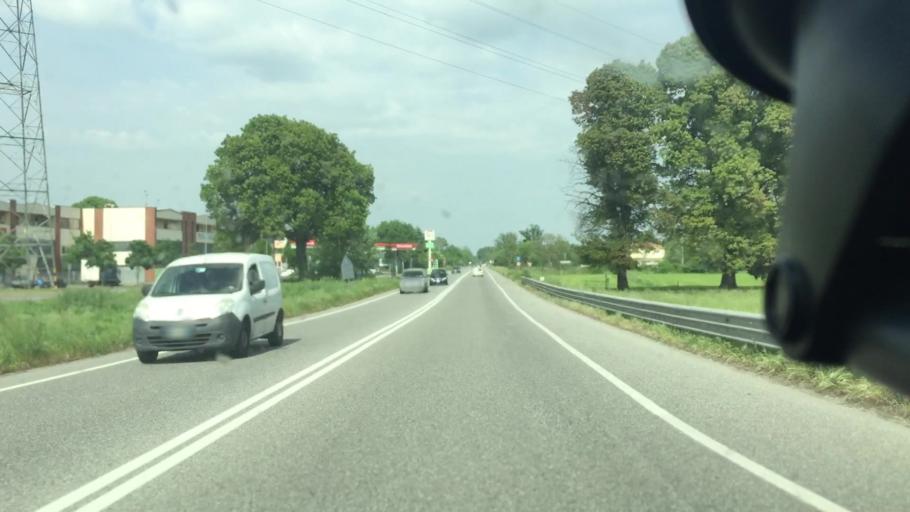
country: IT
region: Lombardy
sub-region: Citta metropolitana di Milano
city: Gorgonzola
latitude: 45.5228
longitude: 9.4059
